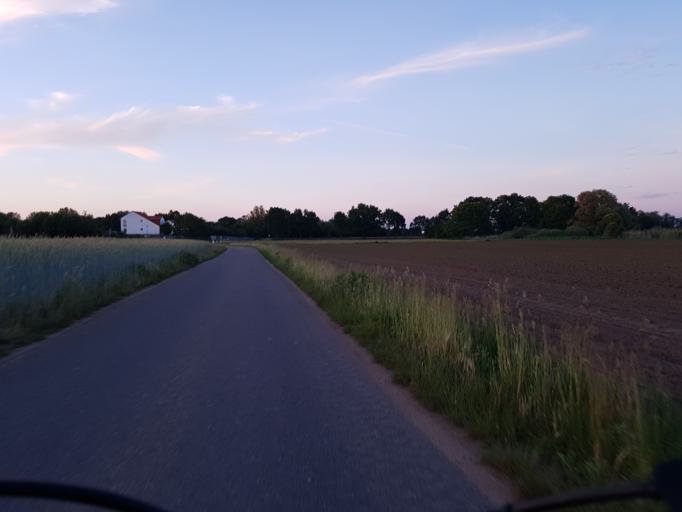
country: DE
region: Brandenburg
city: Falkenberg
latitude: 51.6069
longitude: 13.3037
